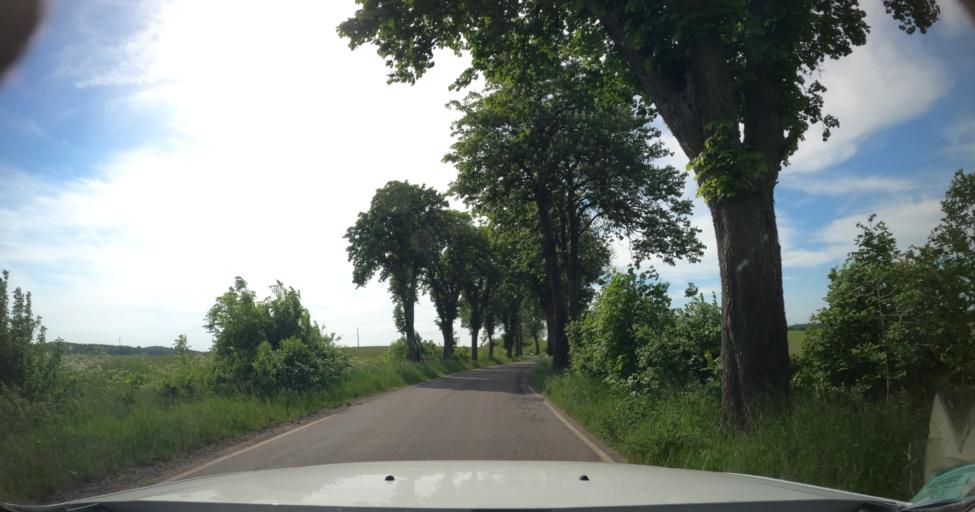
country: PL
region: Warmian-Masurian Voivodeship
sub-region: Powiat ostrodzki
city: Milakowo
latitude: 54.0083
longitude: 20.1363
